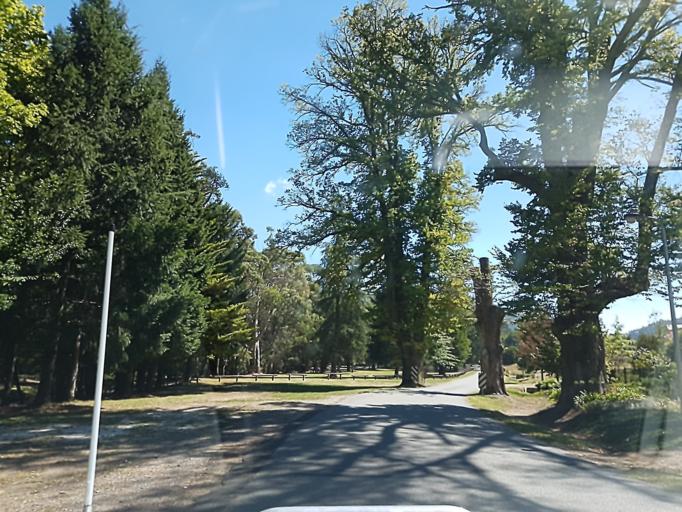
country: AU
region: Victoria
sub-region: Alpine
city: Mount Beauty
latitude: -36.8883
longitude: 147.0643
